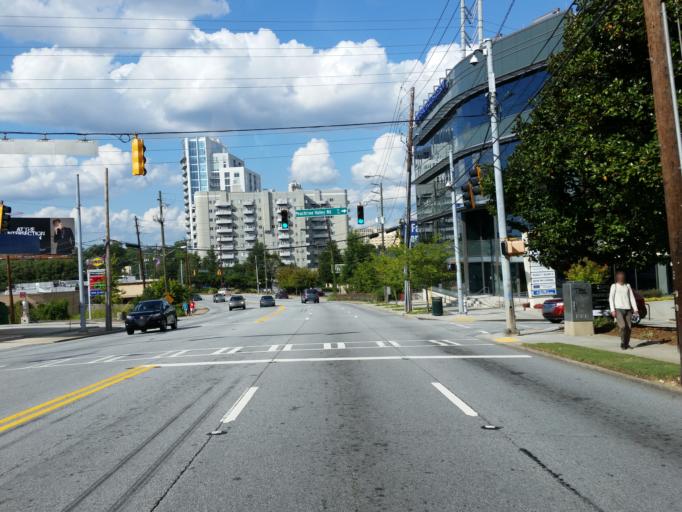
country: US
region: Georgia
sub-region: Fulton County
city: Atlanta
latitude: 33.8106
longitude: -84.3926
